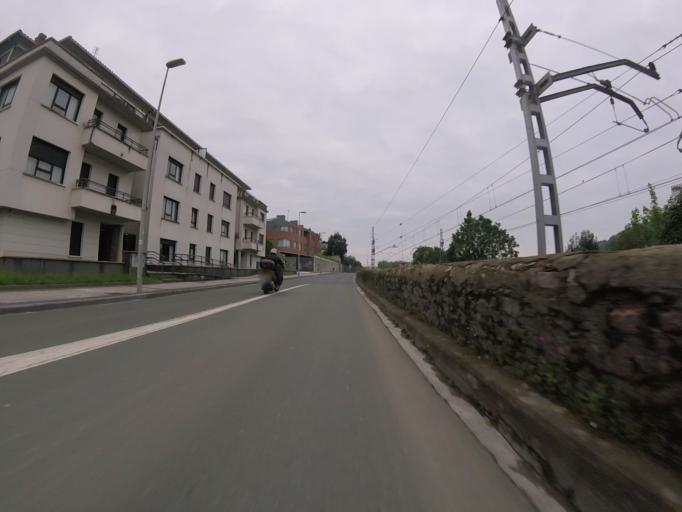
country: ES
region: Basque Country
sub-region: Provincia de Guipuzcoa
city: San Sebastian
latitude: 43.3206
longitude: -1.9624
